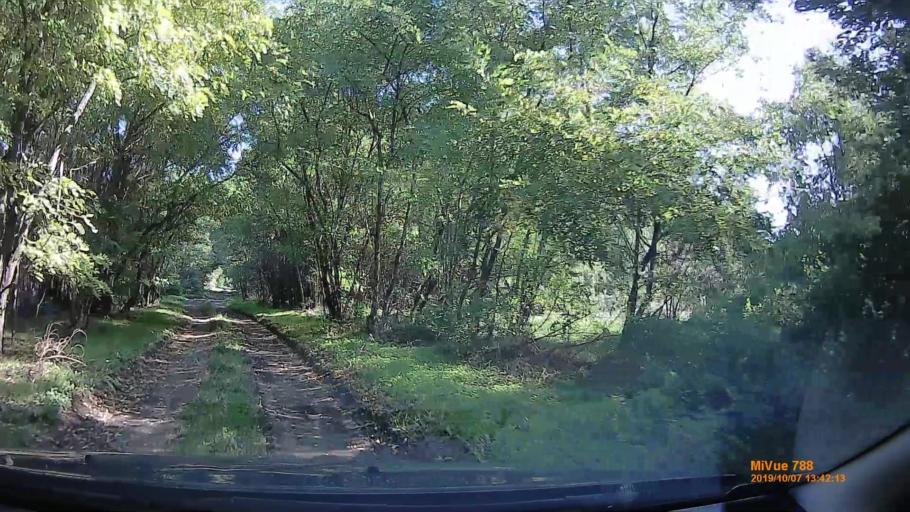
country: HU
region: Jasz-Nagykun-Szolnok
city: Cserkeszolo
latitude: 46.8817
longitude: 20.1951
